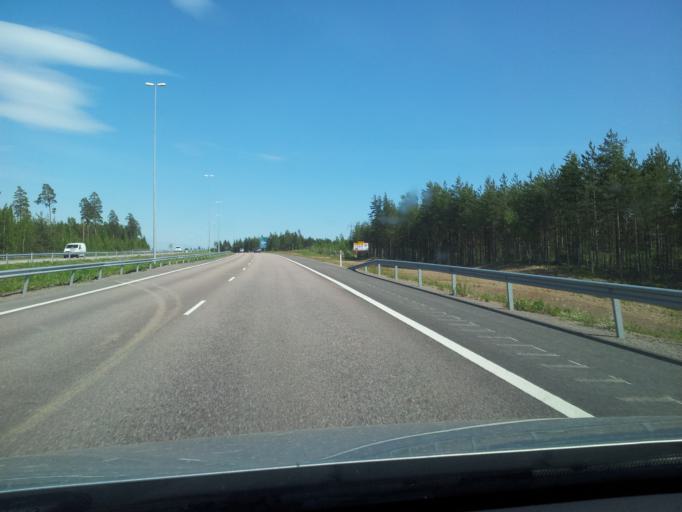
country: FI
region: Uusimaa
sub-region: Loviisa
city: Lovisa
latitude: 60.4588
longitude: 26.1685
